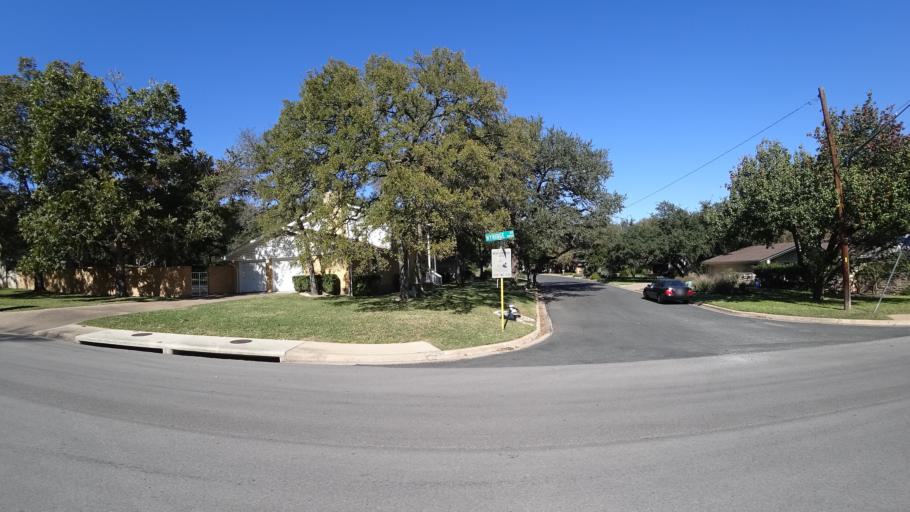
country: US
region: Texas
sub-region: Williamson County
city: Jollyville
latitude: 30.3772
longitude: -97.7452
